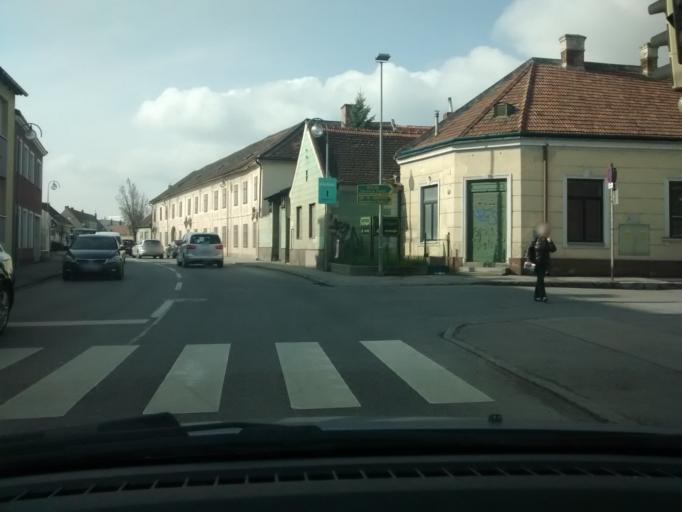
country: AT
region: Lower Austria
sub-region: Politischer Bezirk Baden
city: Traiskirchen
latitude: 48.0169
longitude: 16.2937
